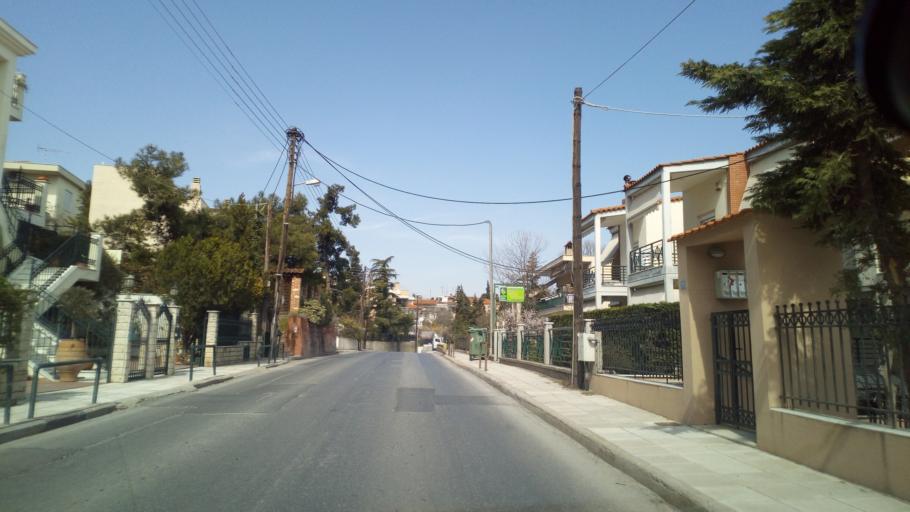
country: GR
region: Central Macedonia
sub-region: Nomos Thessalonikis
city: Panorama
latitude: 40.5873
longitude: 23.0353
